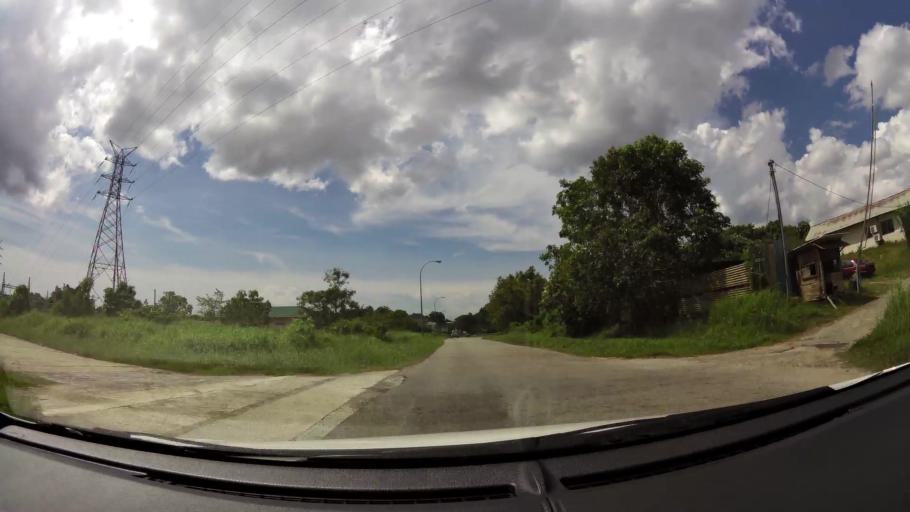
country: BN
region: Brunei and Muara
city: Bandar Seri Begawan
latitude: 4.9489
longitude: 114.9509
